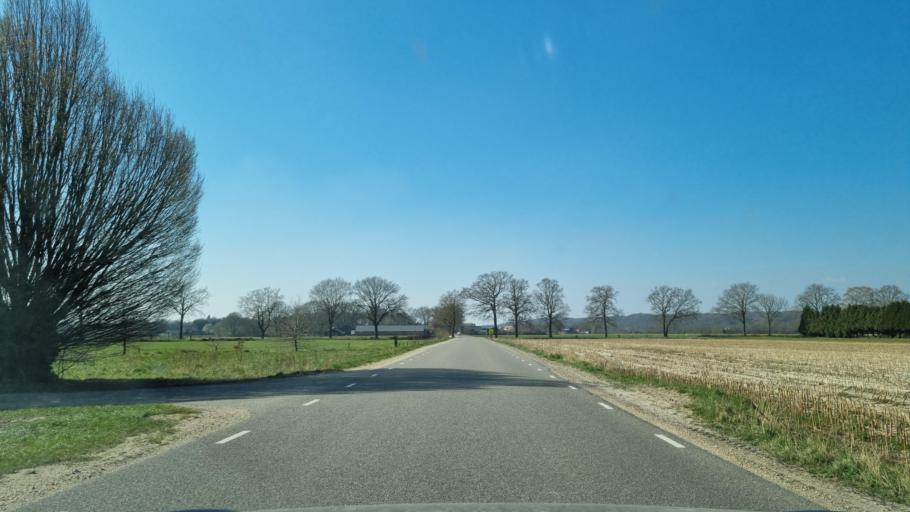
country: NL
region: Limburg
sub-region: Gemeente Gennep
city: Gennep
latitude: 51.7273
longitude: 5.9703
